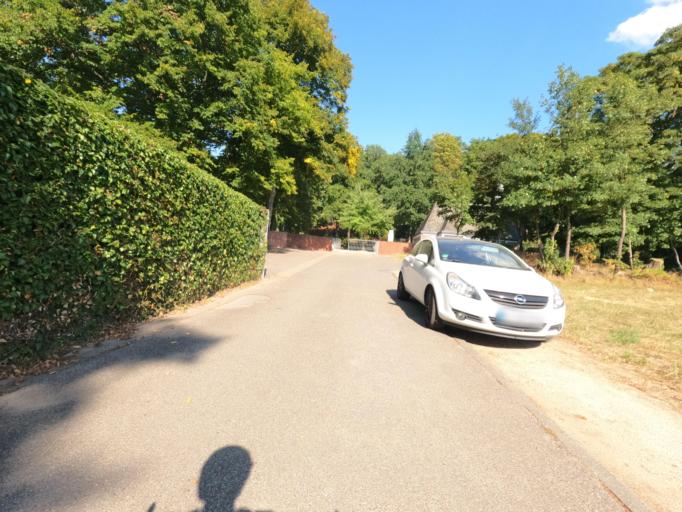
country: DE
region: North Rhine-Westphalia
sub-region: Regierungsbezirk Koln
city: Wassenberg
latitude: 51.0935
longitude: 6.1854
